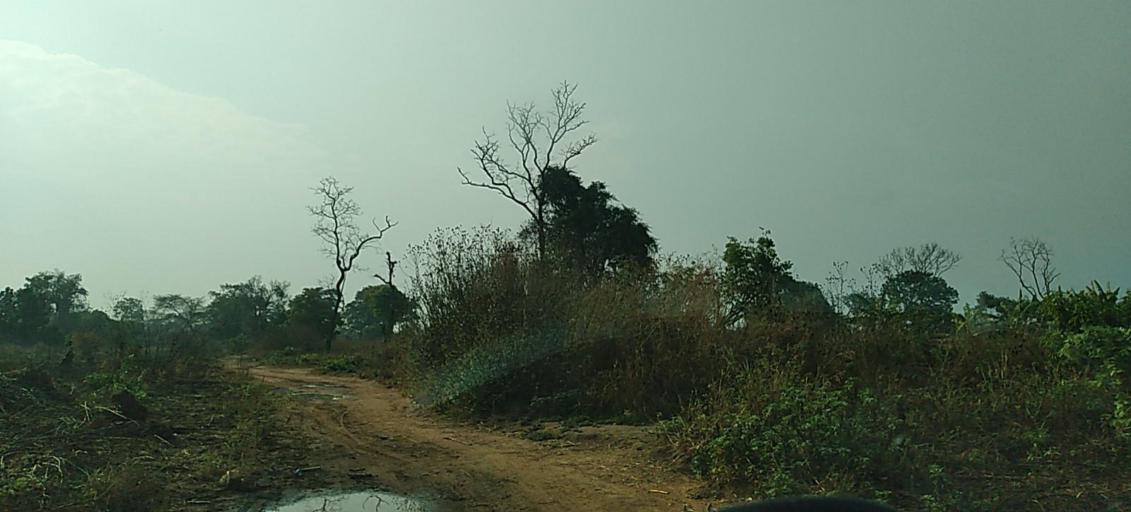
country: ZM
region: North-Western
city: Solwezi
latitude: -12.3551
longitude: 26.5444
